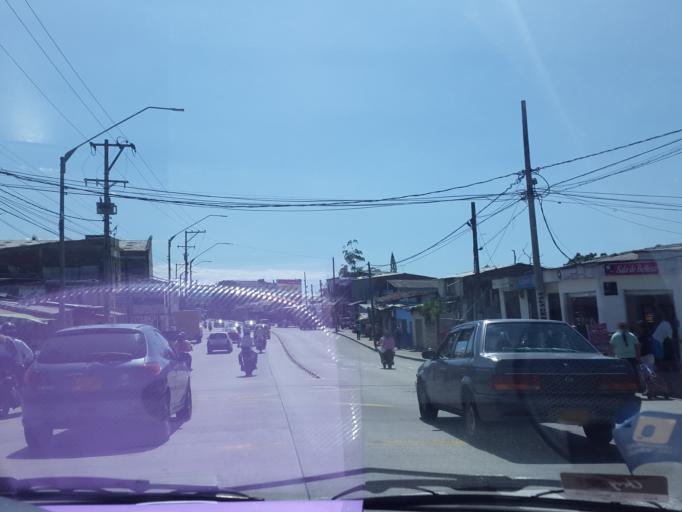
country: CO
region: Quindio
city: Armenia
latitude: 4.5300
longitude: -75.6811
